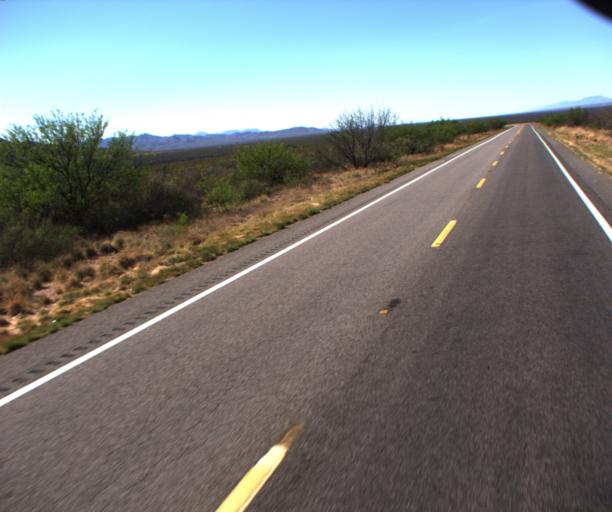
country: US
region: Arizona
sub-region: Cochise County
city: Tombstone
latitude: 31.6228
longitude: -110.0502
